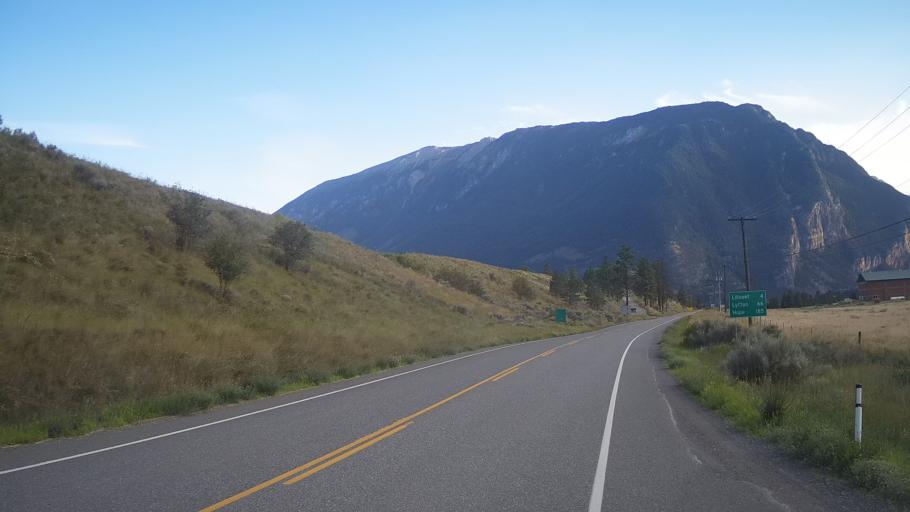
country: CA
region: British Columbia
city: Lillooet
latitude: 50.7008
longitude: -121.9150
